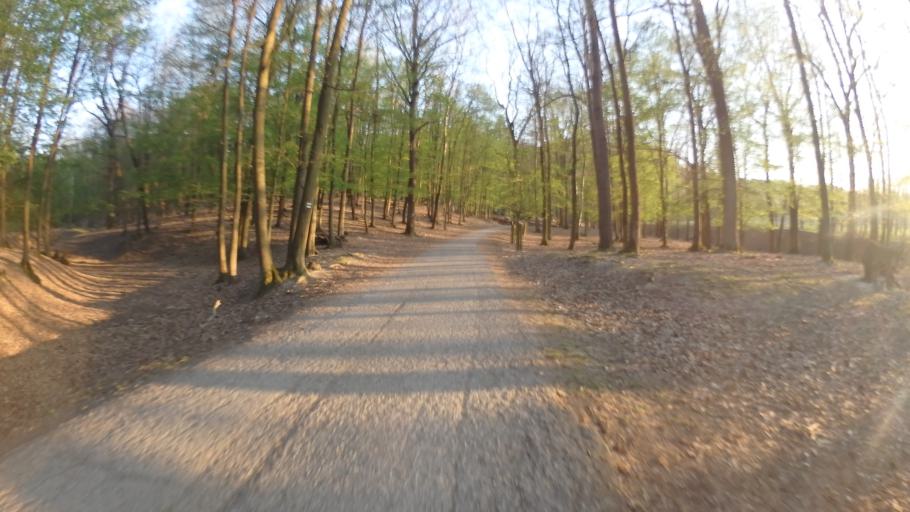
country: CZ
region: South Moravian
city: Troubsko
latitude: 49.2061
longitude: 16.5233
